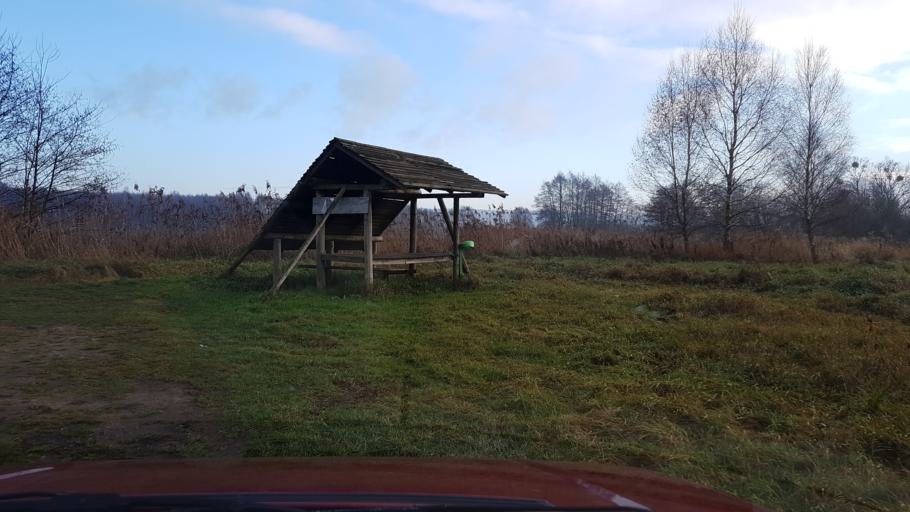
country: PL
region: West Pomeranian Voivodeship
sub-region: Powiat bialogardzki
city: Tychowo
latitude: 53.9859
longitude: 16.3256
